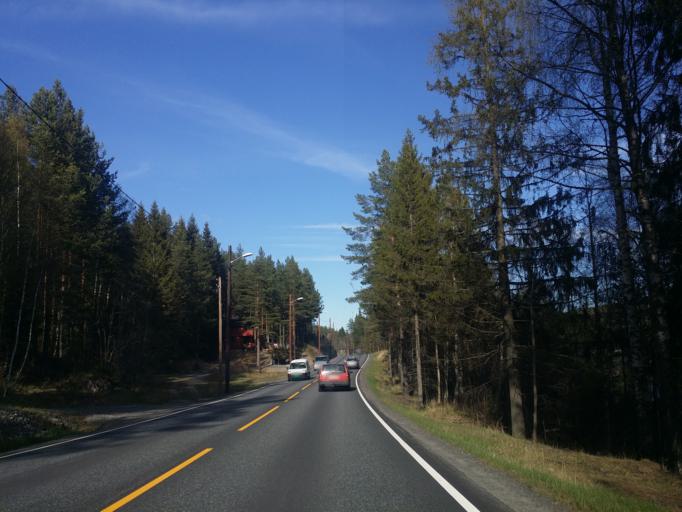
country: NO
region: Buskerud
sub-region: Kongsberg
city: Kongsberg
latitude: 59.6283
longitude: 9.4863
